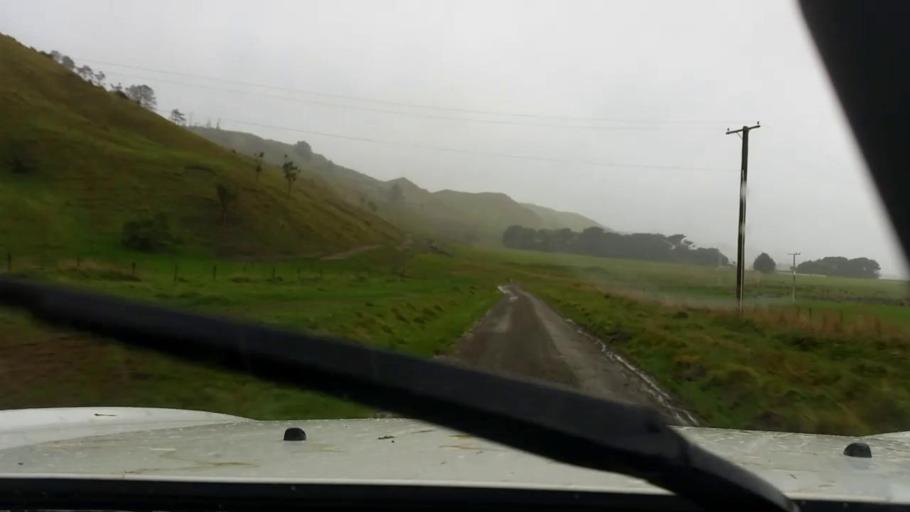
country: NZ
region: Wellington
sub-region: Masterton District
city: Masterton
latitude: -41.2605
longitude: 175.8970
